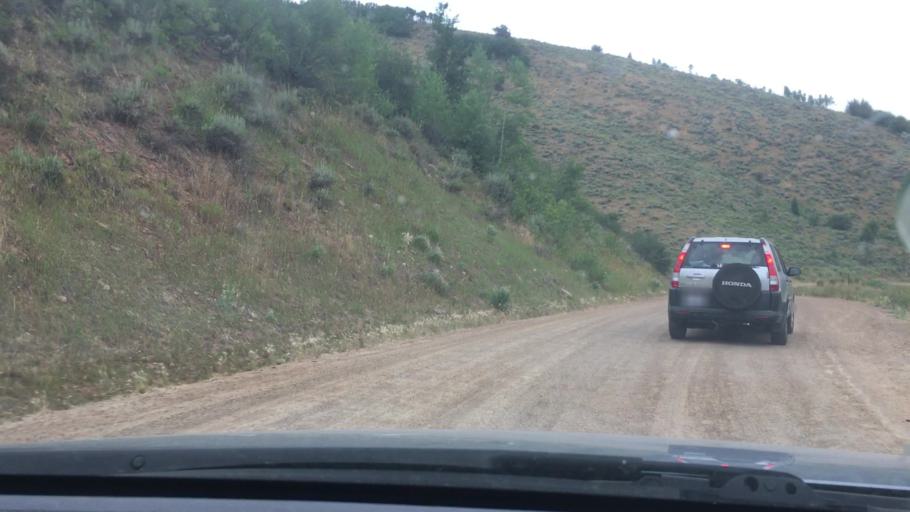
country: US
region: Utah
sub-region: Summit County
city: Summit Park
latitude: 40.7721
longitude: -111.5892
